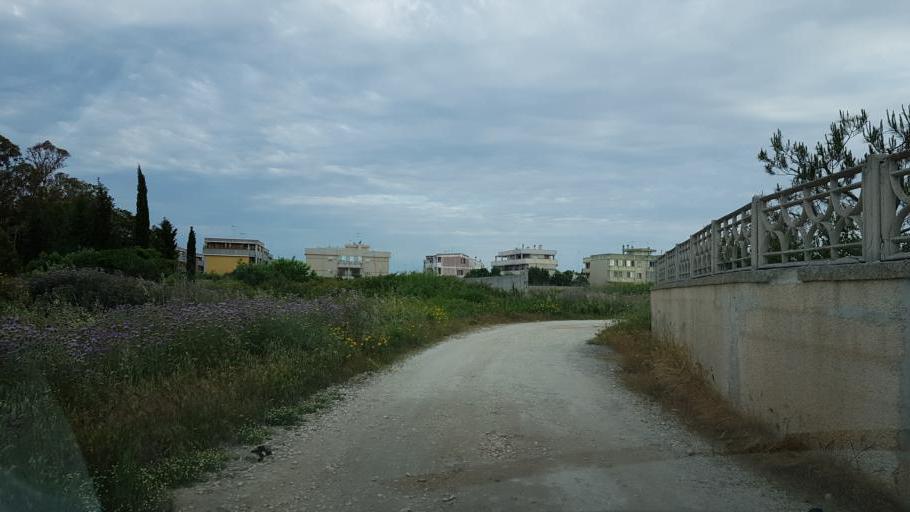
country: IT
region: Apulia
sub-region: Provincia di Brindisi
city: Materdomini
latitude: 40.6579
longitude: 17.9543
